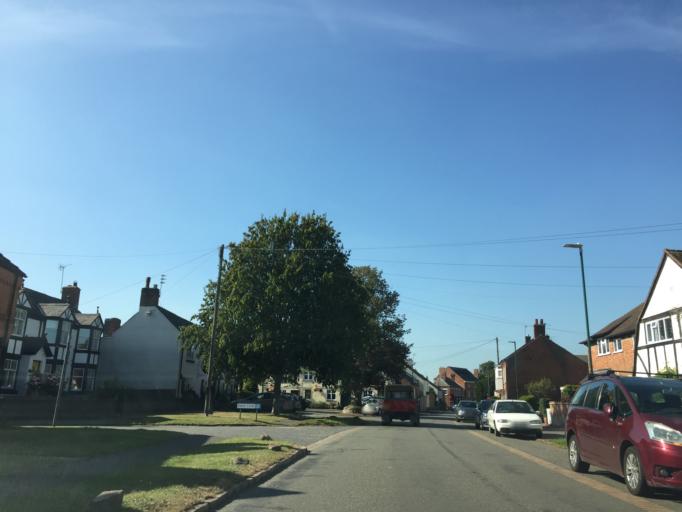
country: GB
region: England
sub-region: Leicestershire
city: Queniborough
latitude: 52.7028
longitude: -1.0413
